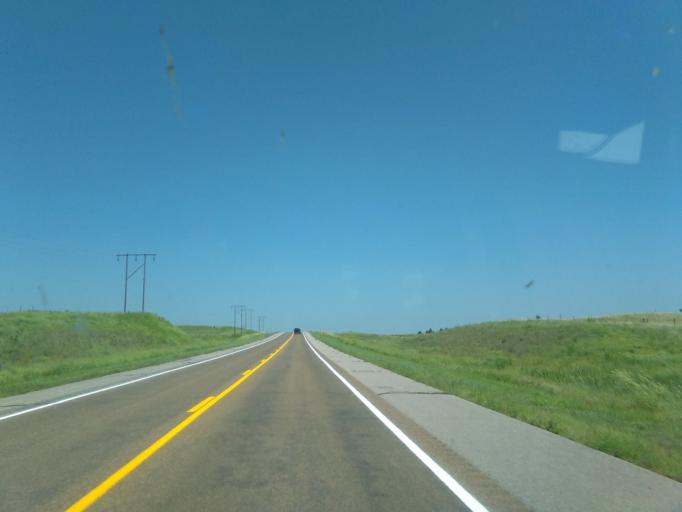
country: US
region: Nebraska
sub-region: Lincoln County
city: North Platte
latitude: 40.8886
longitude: -100.7540
